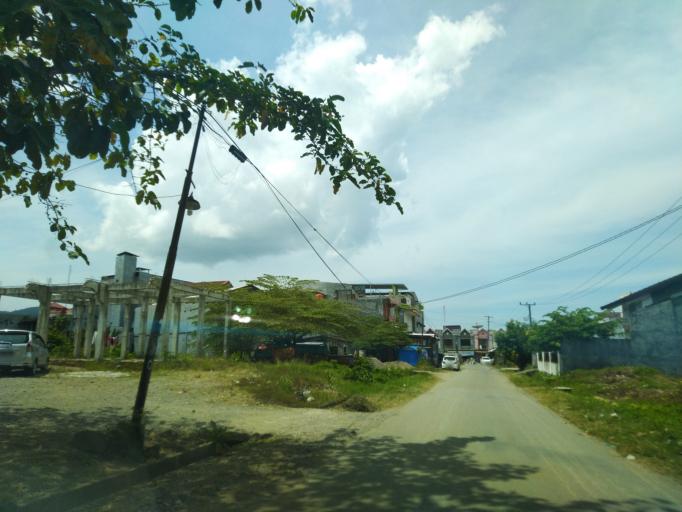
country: ID
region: Sulawesi Barat
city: Mamuju
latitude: -2.6887
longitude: 118.8788
